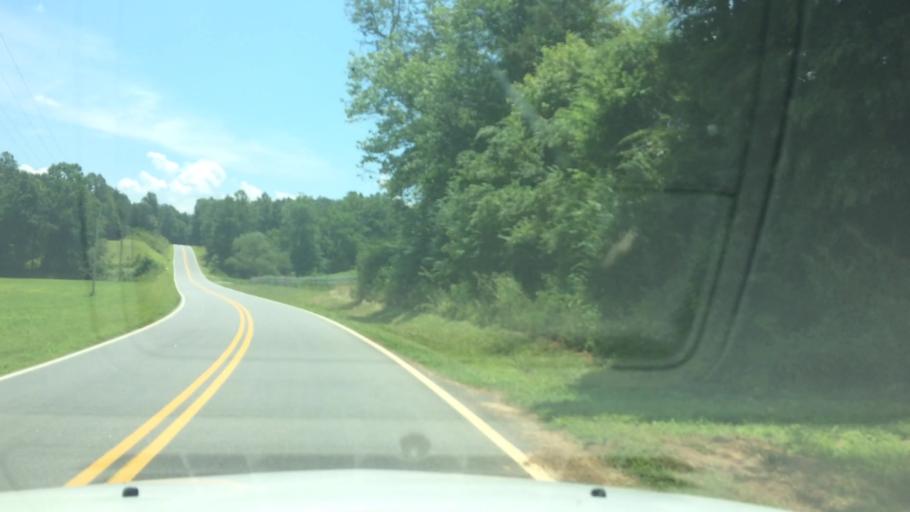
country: US
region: North Carolina
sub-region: Alexander County
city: Taylorsville
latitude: 35.9586
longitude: -81.2692
